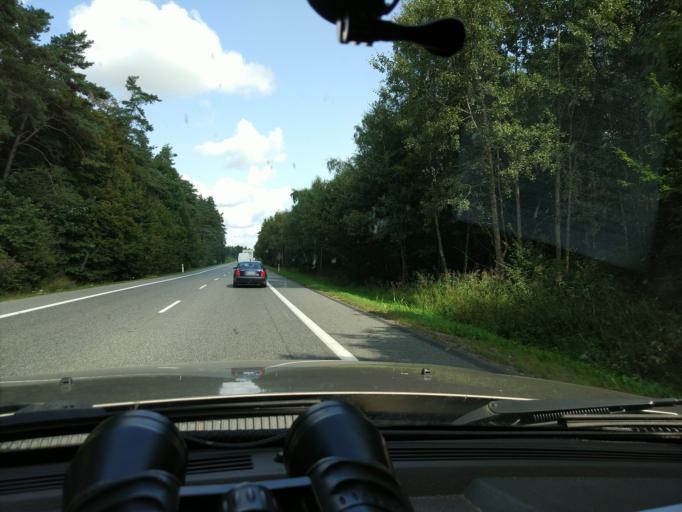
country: PL
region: Masovian Voivodeship
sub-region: Powiat mlawski
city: Mlawa
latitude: 53.1364
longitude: 20.3966
